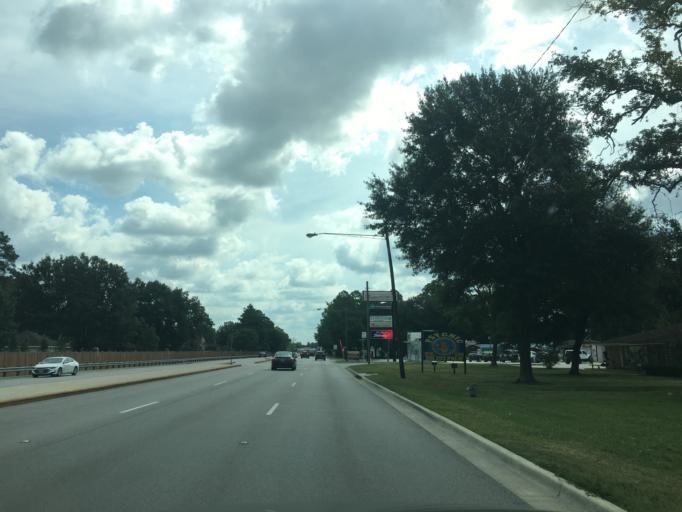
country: US
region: Texas
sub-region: Harris County
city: Spring
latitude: 30.1246
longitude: -95.4162
